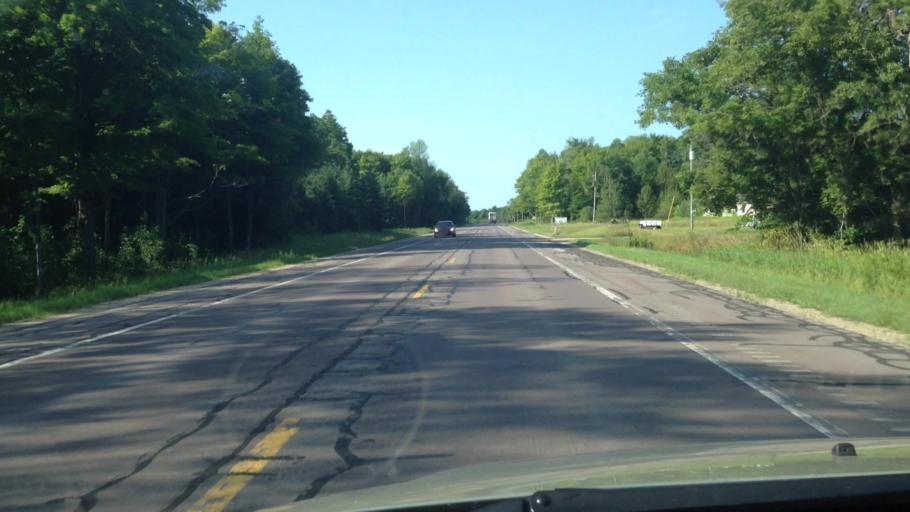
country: US
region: Michigan
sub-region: Schoolcraft County
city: Manistique
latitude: 46.0905
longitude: -85.9515
